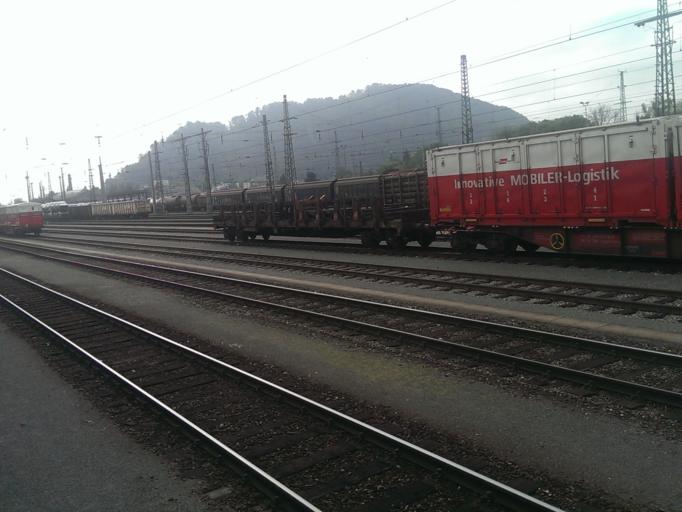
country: AT
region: Salzburg
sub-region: Salzburg Stadt
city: Salzburg
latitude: 47.8180
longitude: 13.0636
